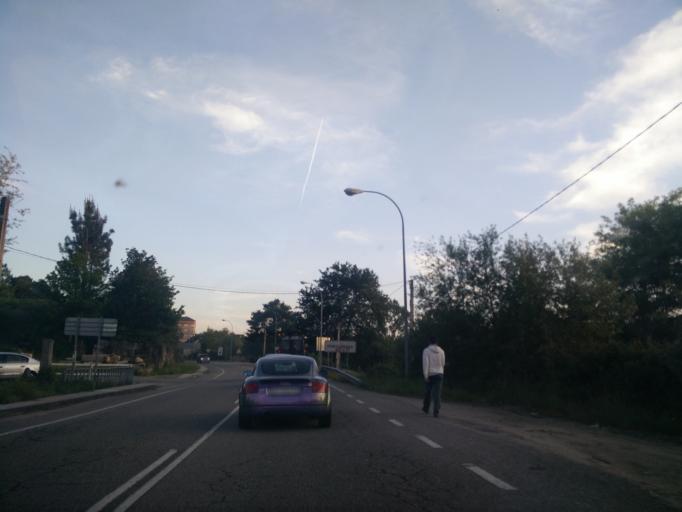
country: ES
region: Galicia
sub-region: Provincia de Pontevedra
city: Ponteareas
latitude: 42.1804
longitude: -8.5084
